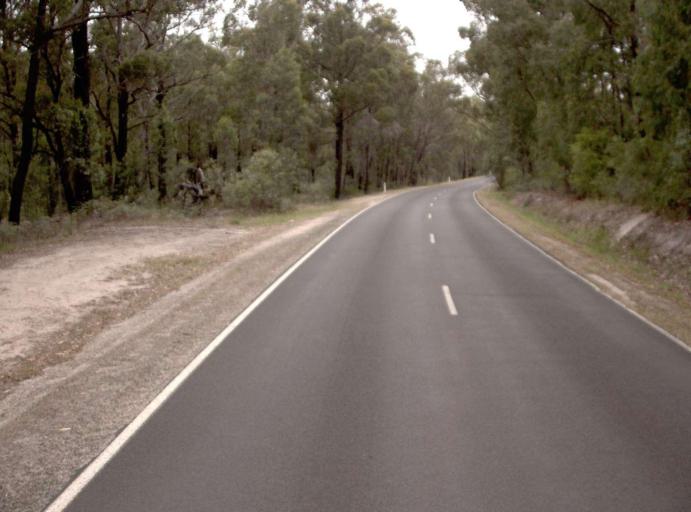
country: AU
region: Victoria
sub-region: Latrobe
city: Traralgon
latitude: -38.4712
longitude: 146.8228
